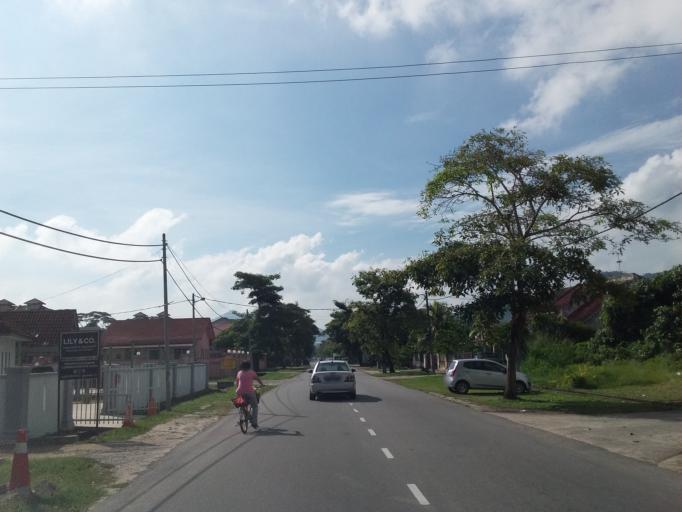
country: MY
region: Johor
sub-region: Daerah Batu Pahat
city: Batu Pahat
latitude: 1.8431
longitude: 102.9247
